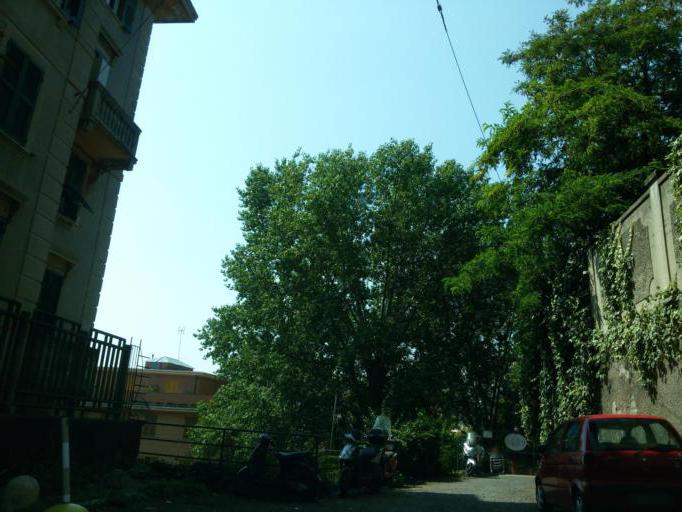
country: IT
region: Liguria
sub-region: Provincia di Genova
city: Genoa
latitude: 44.4069
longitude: 8.9672
